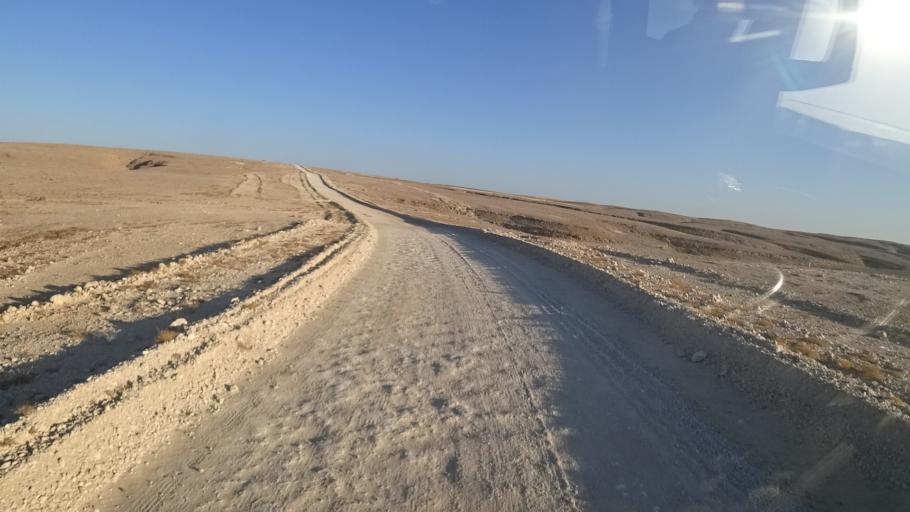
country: YE
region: Al Mahrah
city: Hawf
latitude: 17.1759
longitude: 53.3443
